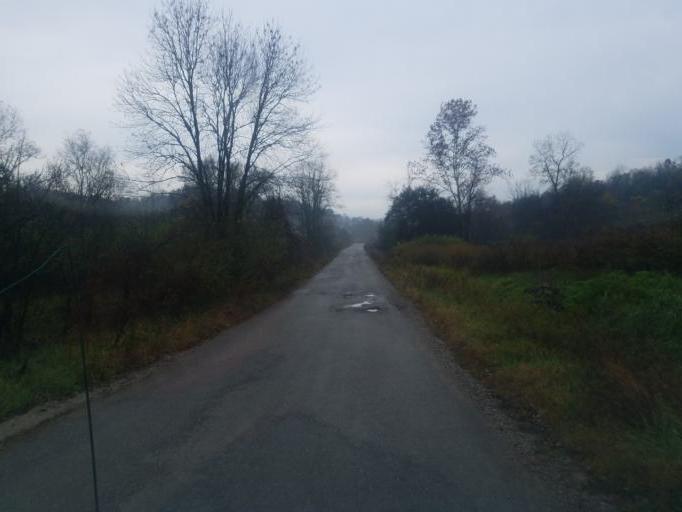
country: US
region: Ohio
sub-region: Athens County
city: Glouster
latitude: 39.5149
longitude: -81.9484
